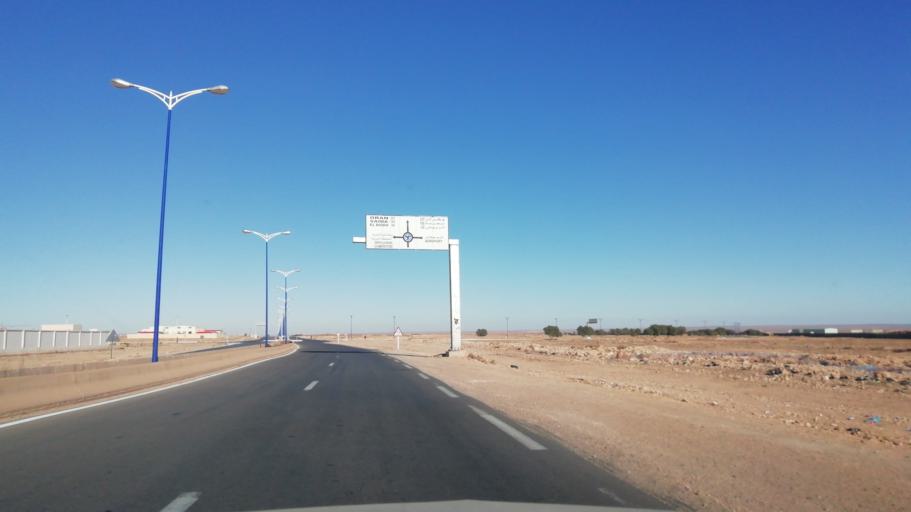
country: DZ
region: Wilaya de Naama
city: Naama
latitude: 33.5408
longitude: -0.2554
